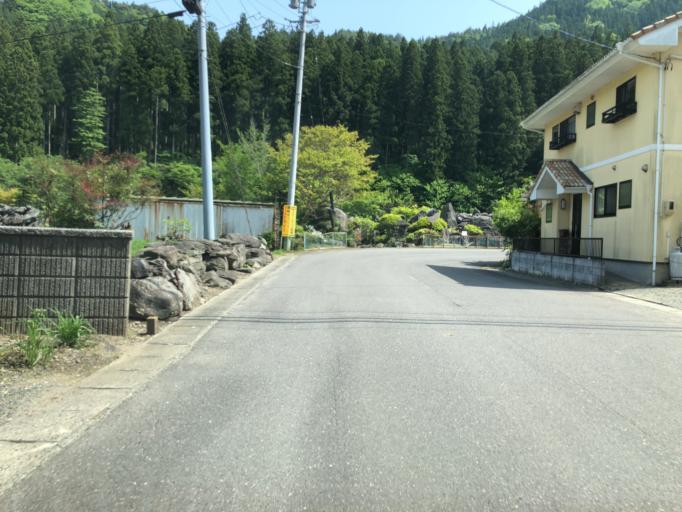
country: JP
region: Fukushima
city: Ishikawa
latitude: 37.0546
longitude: 140.5862
